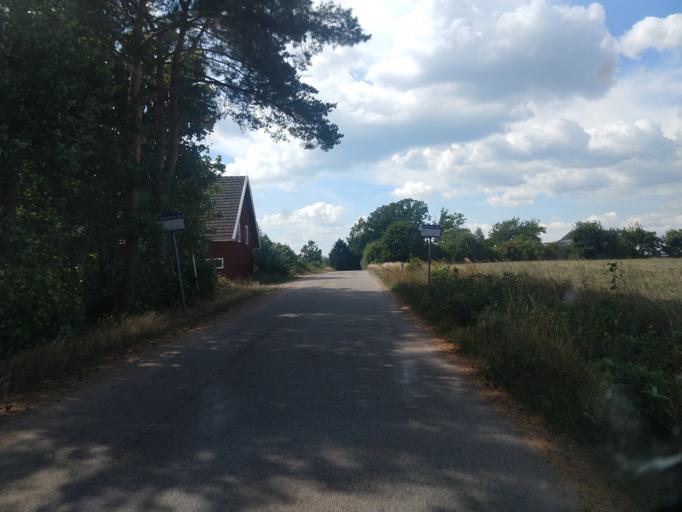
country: SE
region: Blekinge
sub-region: Karlskrona Kommun
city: Nattraby
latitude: 56.2456
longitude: 15.5418
